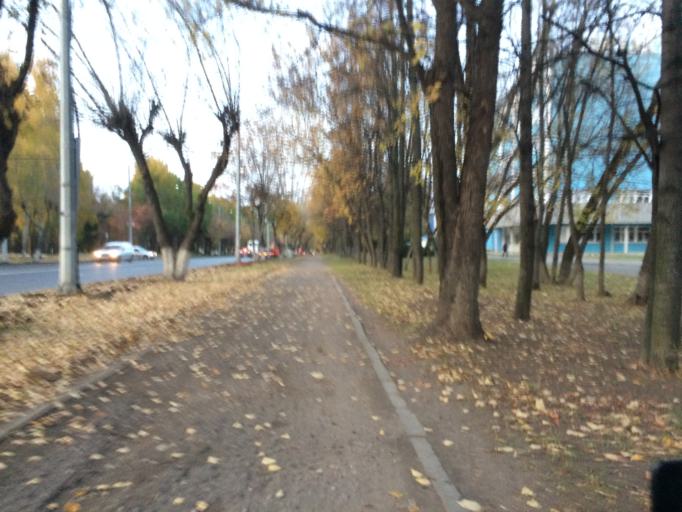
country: RU
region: Mariy-El
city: Yoshkar-Ola
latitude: 56.6110
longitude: 47.8801
